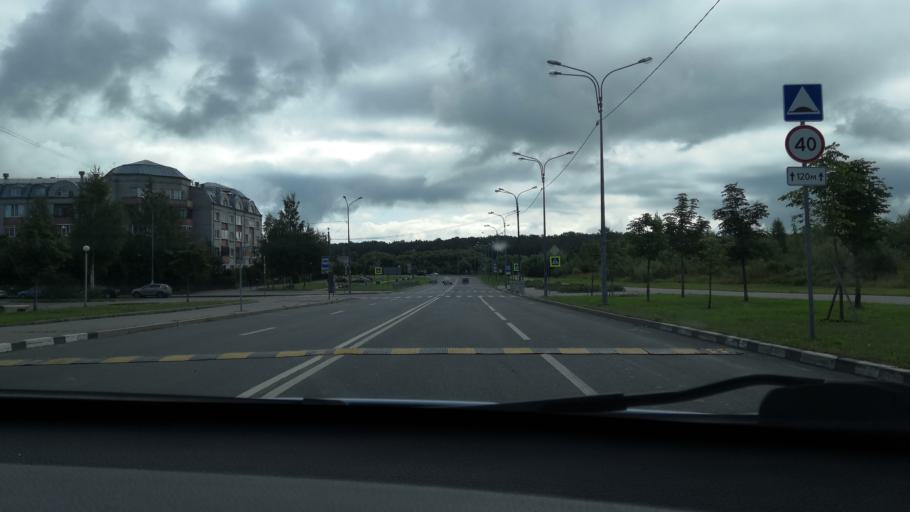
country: RU
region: St.-Petersburg
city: Pavlovsk
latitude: 59.6939
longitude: 30.4237
